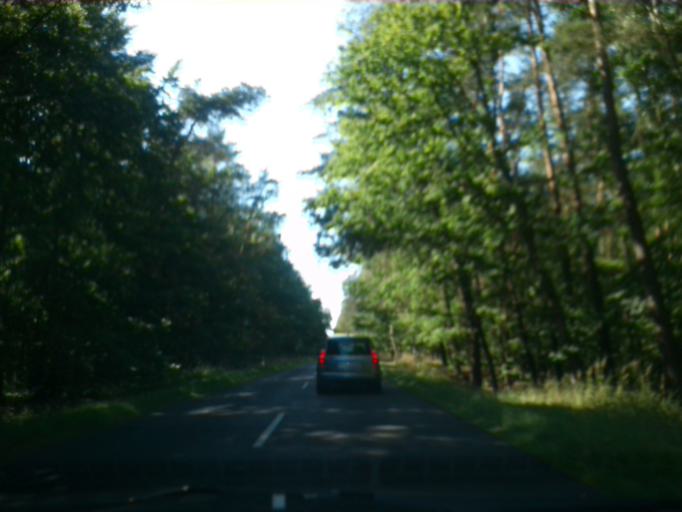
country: PL
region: West Pomeranian Voivodeship
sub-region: Powiat goleniowski
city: Stepnica
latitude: 53.6285
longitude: 14.6771
